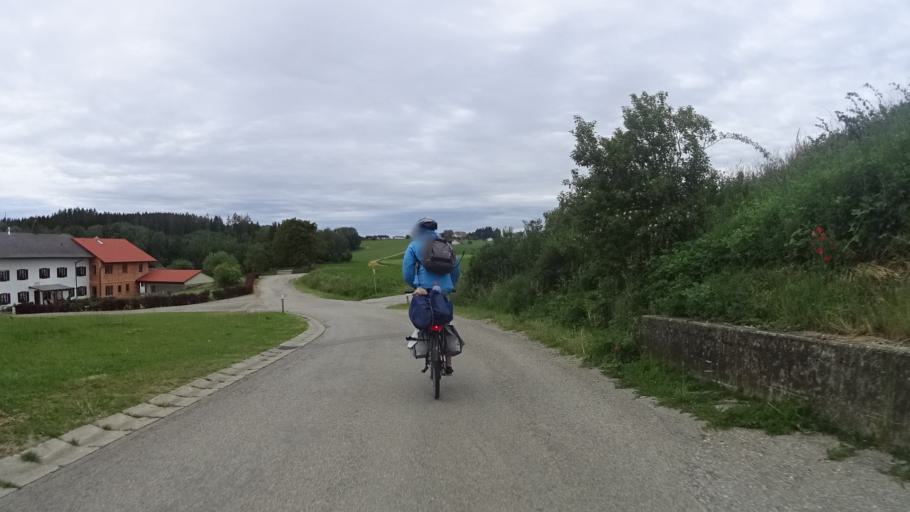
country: DE
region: Bavaria
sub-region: Lower Bavaria
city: Wurmsham
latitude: 48.3884
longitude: 12.3234
